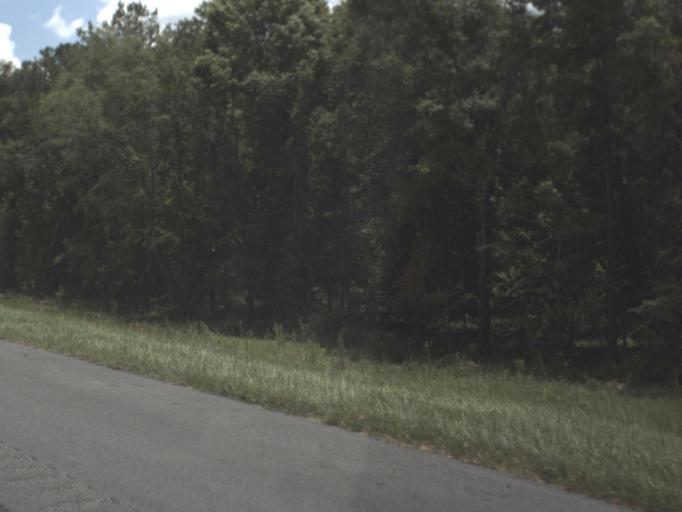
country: US
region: Florida
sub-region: Suwannee County
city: Live Oak
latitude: 30.3585
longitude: -83.1975
